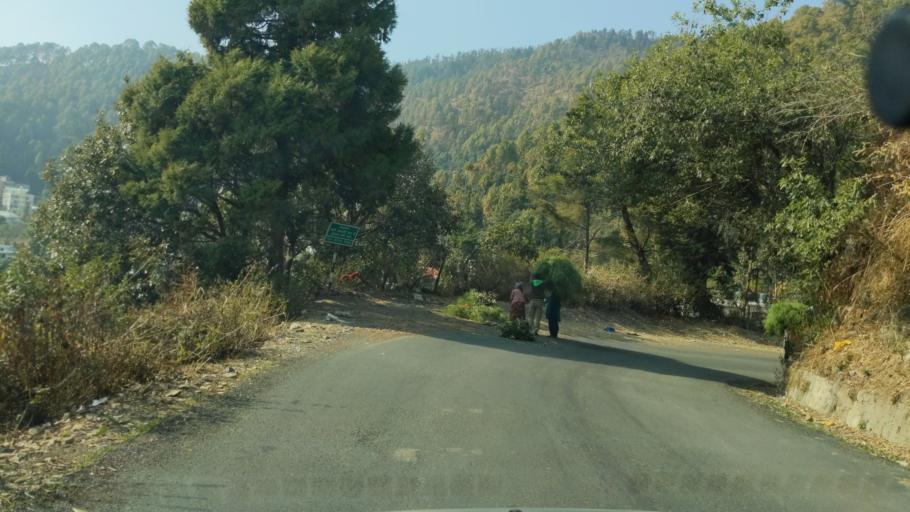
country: IN
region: Uttarakhand
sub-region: Naini Tal
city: Bhowali
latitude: 29.3913
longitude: 79.5338
